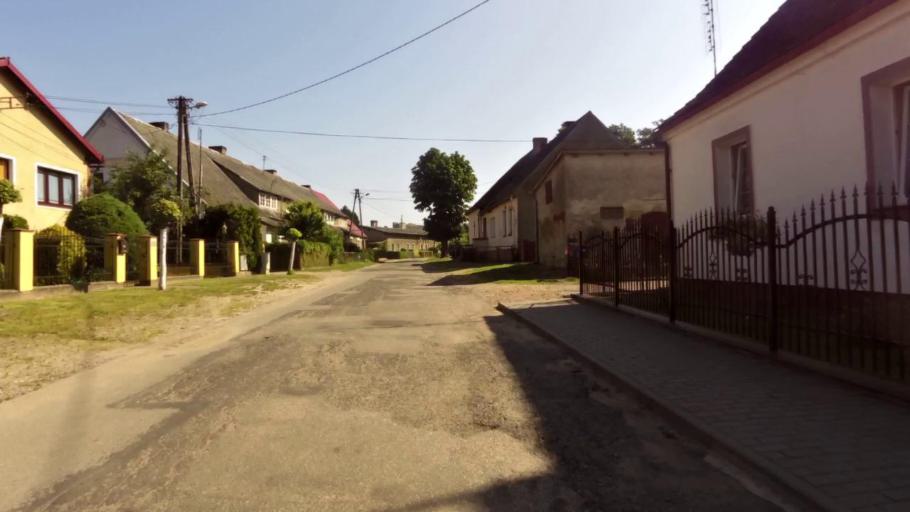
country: PL
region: West Pomeranian Voivodeship
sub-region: Powiat swidwinski
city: Rabino
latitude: 53.8923
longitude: 16.0678
